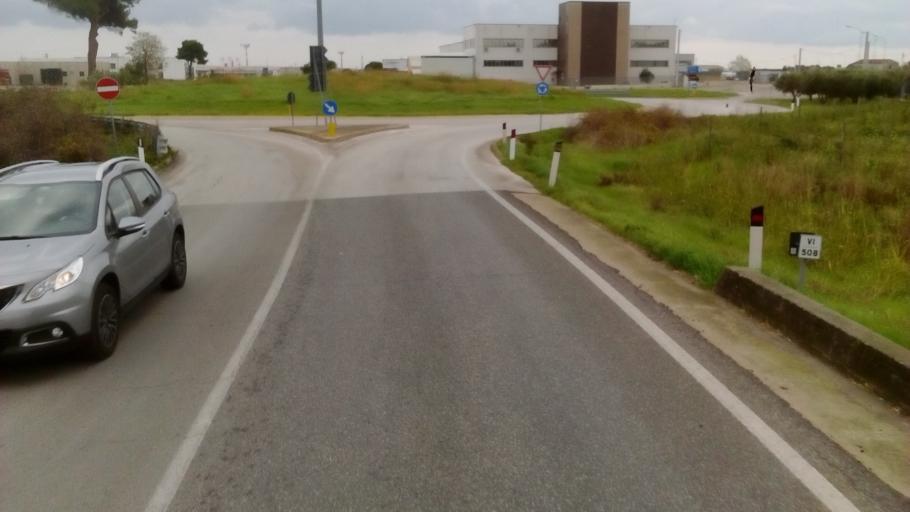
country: IT
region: Abruzzo
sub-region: Provincia di Chieti
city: Vasto
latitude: 42.1656
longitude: 14.6814
